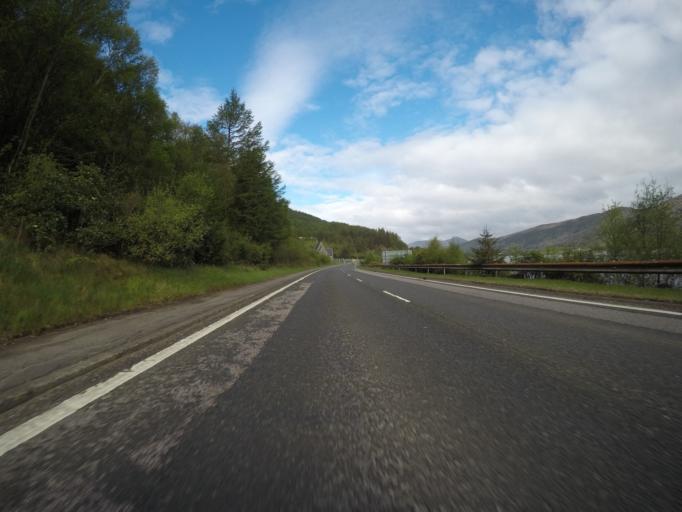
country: GB
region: Scotland
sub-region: Highland
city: Fort William
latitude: 56.6774
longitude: -5.1520
